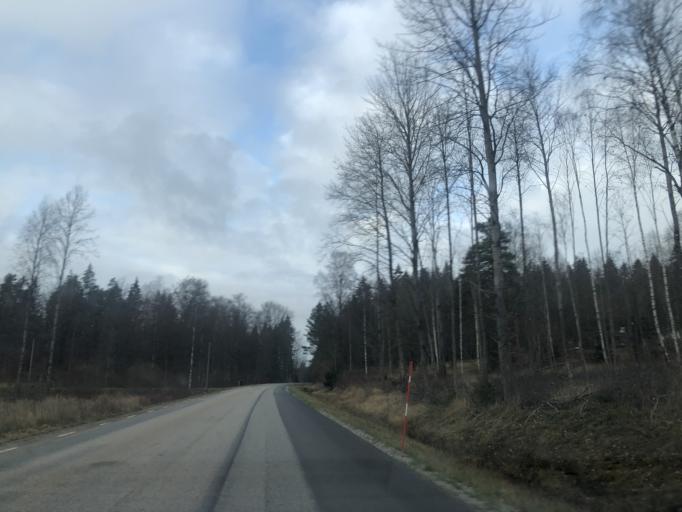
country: SE
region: Vaestra Goetaland
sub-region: Tranemo Kommun
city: Langhem
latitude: 57.7106
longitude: 13.2982
